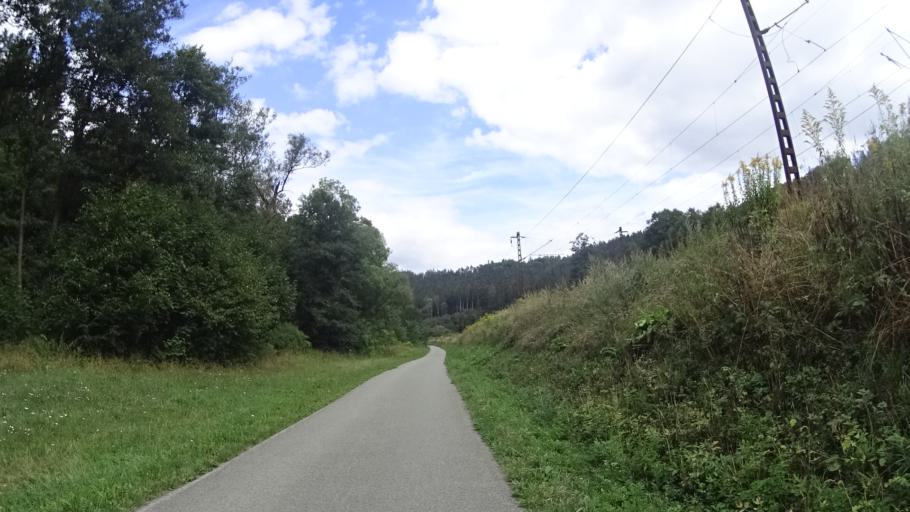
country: CZ
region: Pardubicky
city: Brandys nad Orlici
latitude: 49.9794
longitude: 16.3348
